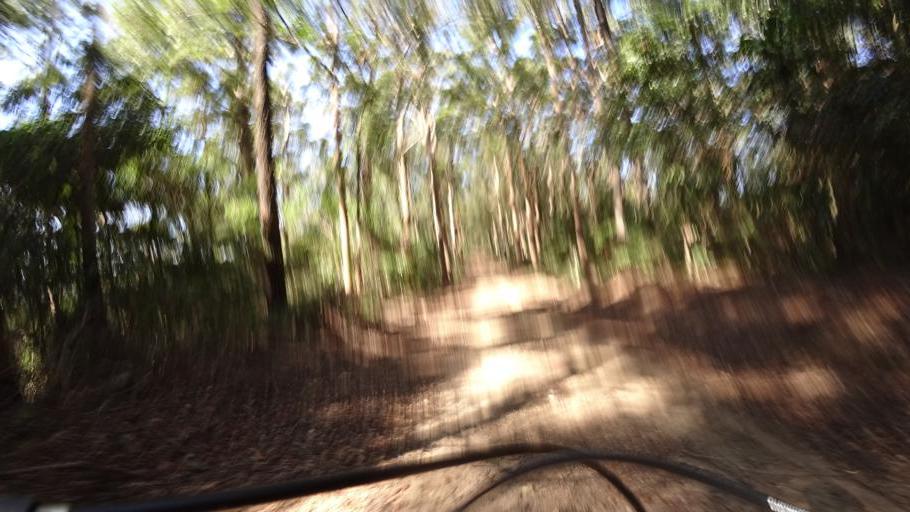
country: AU
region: Queensland
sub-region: Moreton Bay
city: Highvale
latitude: -27.4066
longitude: 152.7794
